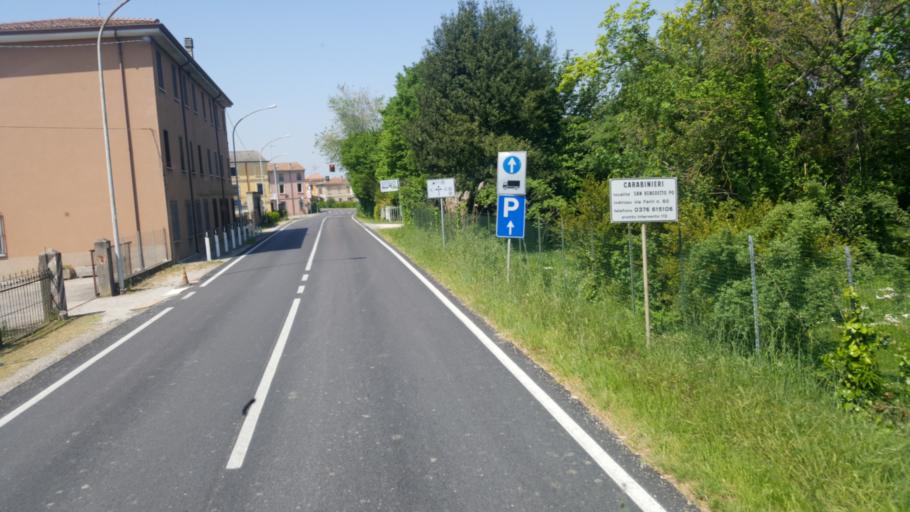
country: IT
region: Lombardy
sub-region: Provincia di Mantova
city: San Benedetto Po
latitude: 45.0383
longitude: 10.9293
